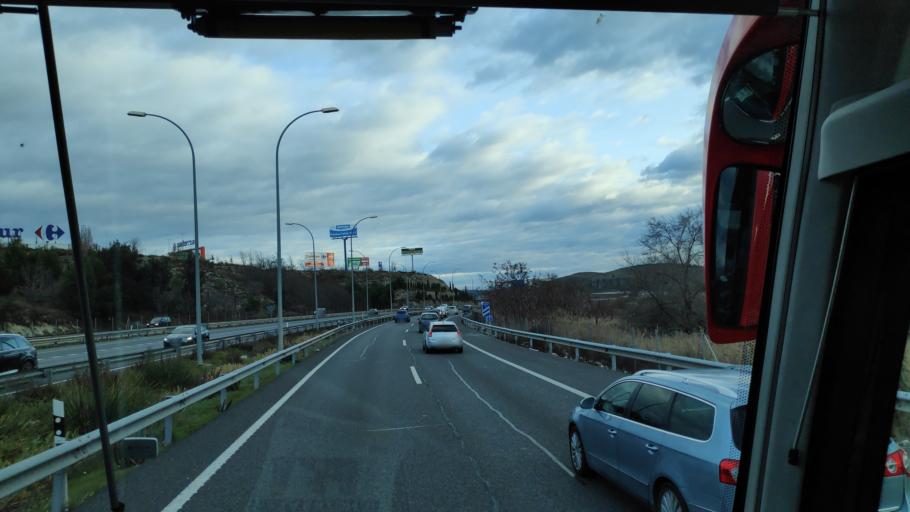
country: ES
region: Madrid
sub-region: Provincia de Madrid
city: Vaciamadrid
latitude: 40.3430
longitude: -3.5398
